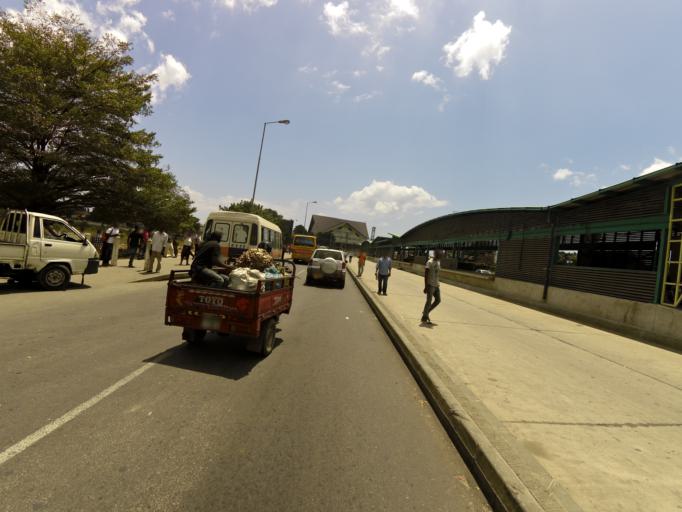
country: TZ
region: Dar es Salaam
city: Magomeni
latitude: -6.8062
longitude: 39.2581
